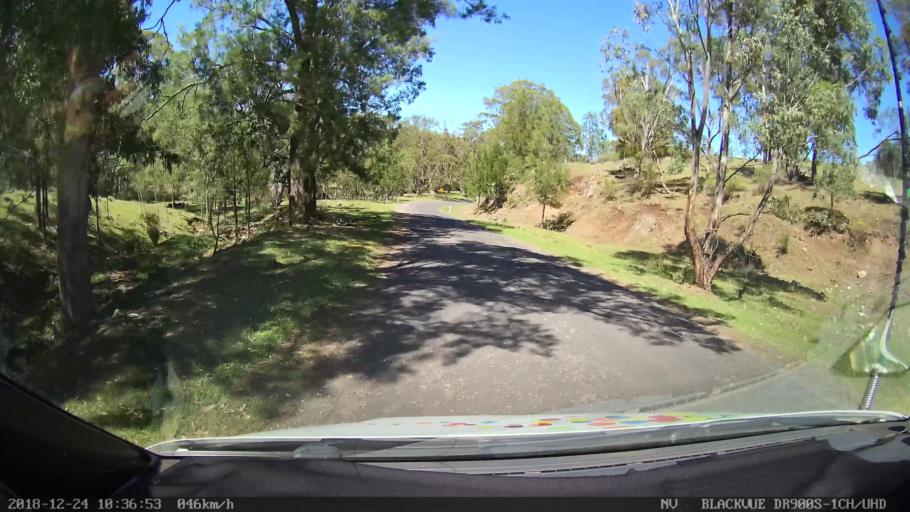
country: AU
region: New South Wales
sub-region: Upper Hunter Shire
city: Merriwa
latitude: -31.8454
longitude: 150.4969
